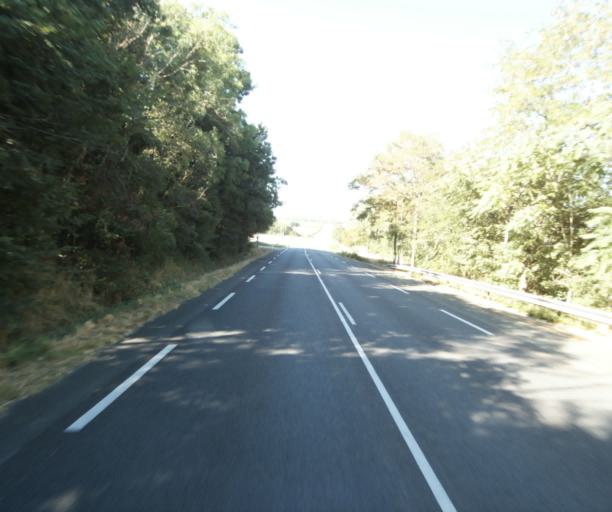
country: FR
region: Midi-Pyrenees
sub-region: Departement du Tarn
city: Soreze
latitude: 43.4970
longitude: 2.0449
